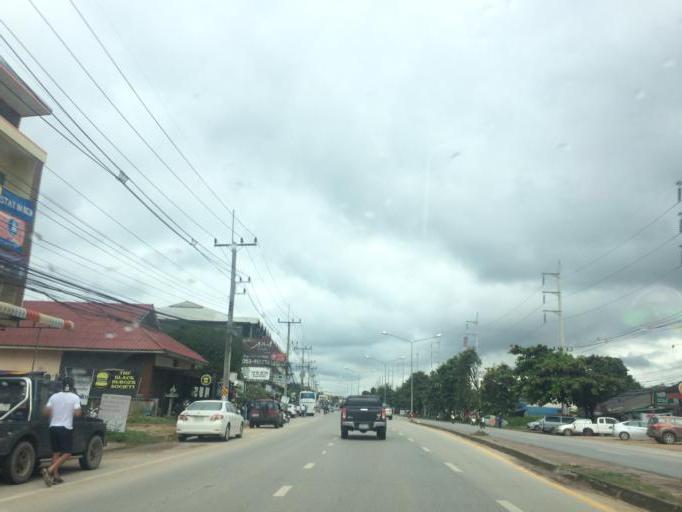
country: TH
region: Chiang Rai
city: Mae Chan
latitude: 20.0495
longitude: 99.8759
